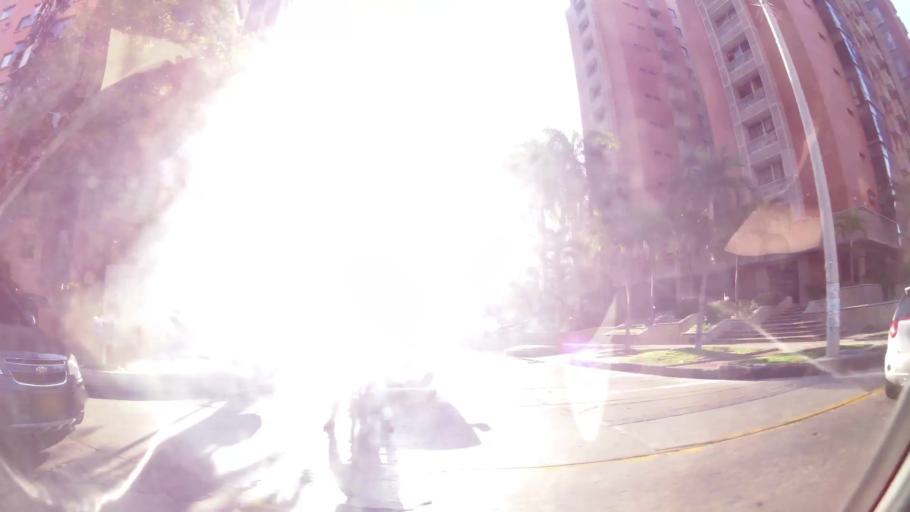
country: CO
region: Atlantico
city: Barranquilla
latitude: 11.0079
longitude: -74.8121
